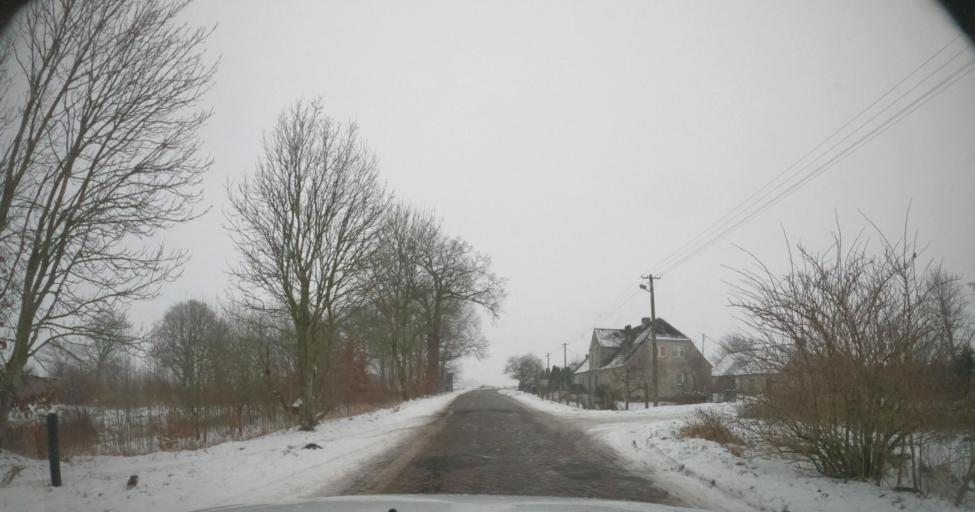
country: PL
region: West Pomeranian Voivodeship
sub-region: Powiat gryficki
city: Brojce
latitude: 53.9010
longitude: 15.3746
